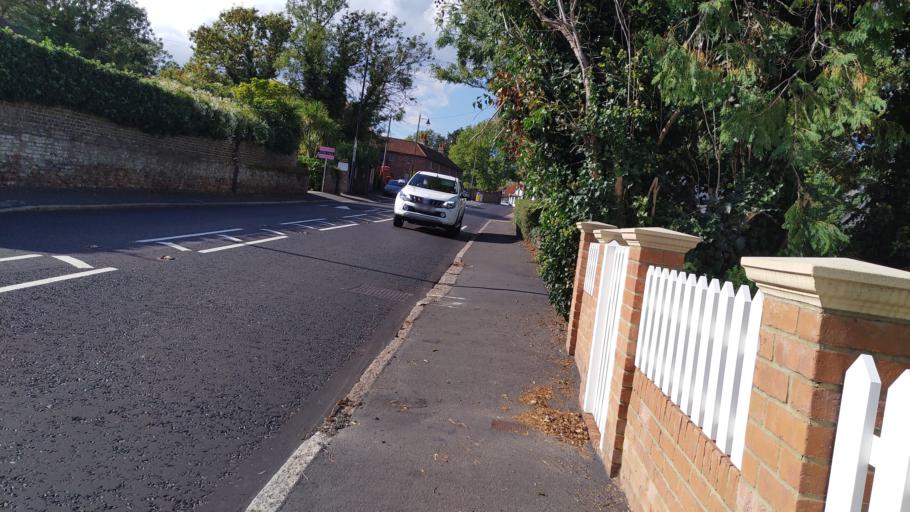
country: GB
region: England
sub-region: Hertfordshire
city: Potters Bar
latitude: 51.7041
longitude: -0.1494
